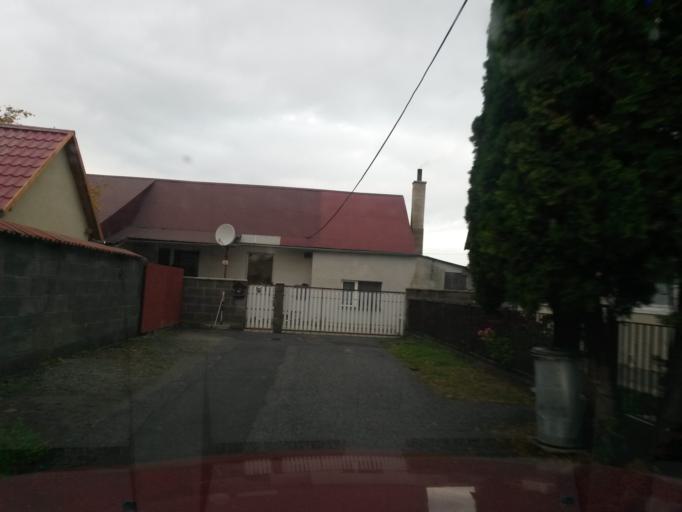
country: SK
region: Kosicky
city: Kosice
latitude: 48.7912
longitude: 21.2413
